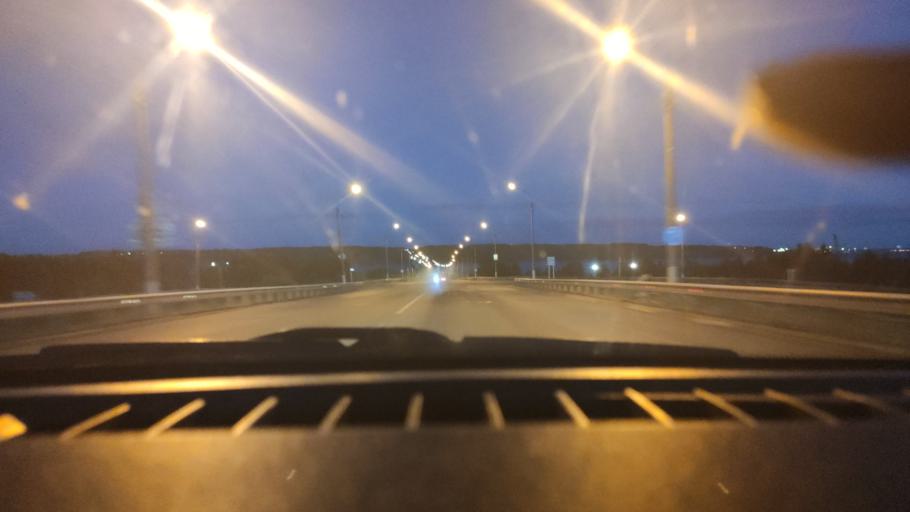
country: RU
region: Perm
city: Polazna
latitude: 58.1759
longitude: 56.4140
